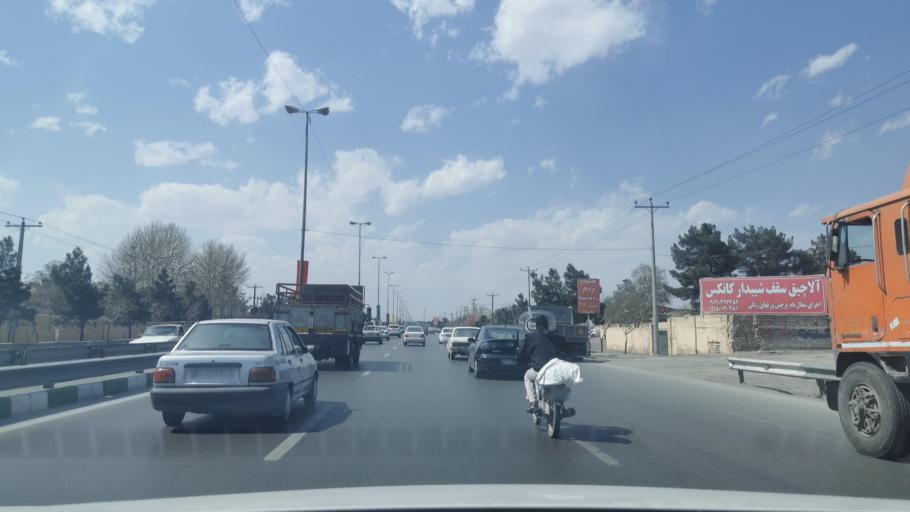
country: IR
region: Razavi Khorasan
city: Mashhad
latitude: 36.3925
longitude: 59.5042
